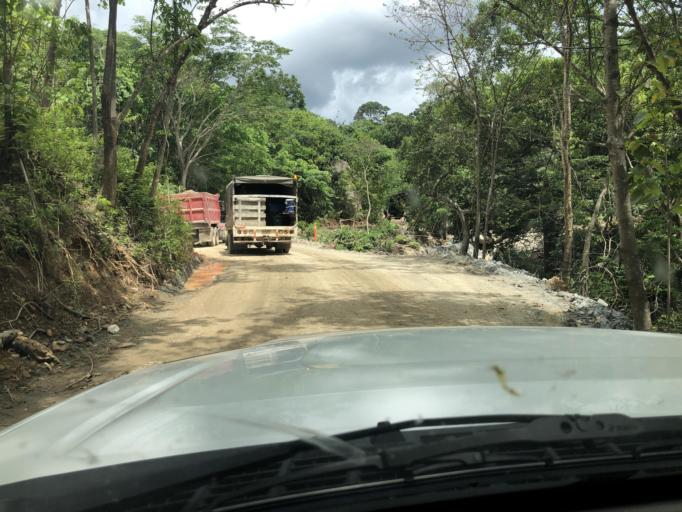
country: MX
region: Jalisco
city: Purificacion
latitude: 19.7457
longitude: -104.5136
